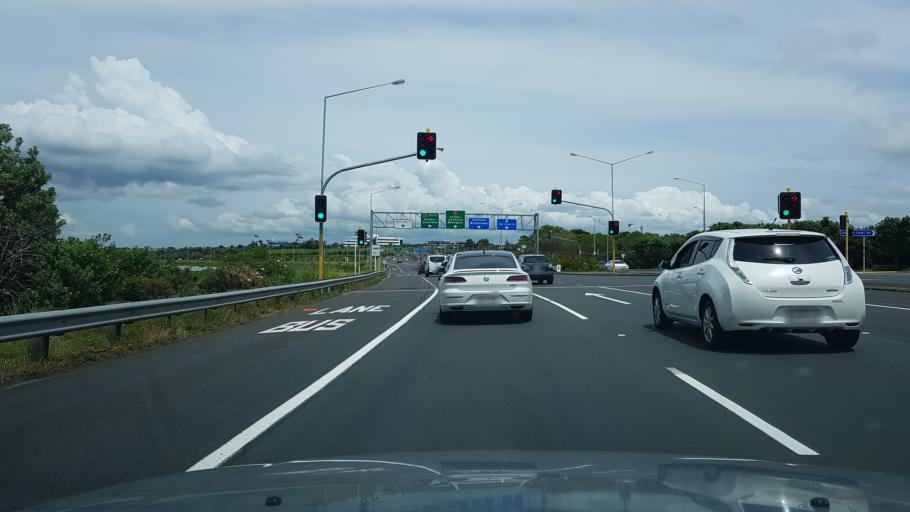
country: NZ
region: Auckland
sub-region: Auckland
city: North Shore
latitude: -36.7964
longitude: 174.7666
